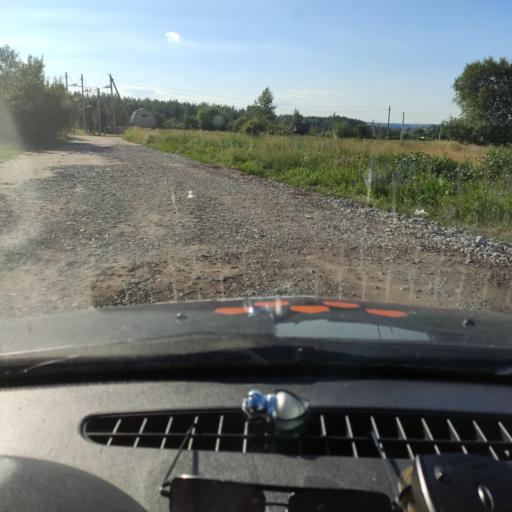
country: RU
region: Voronezj
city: Podgornoye
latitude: 51.8649
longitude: 39.1749
